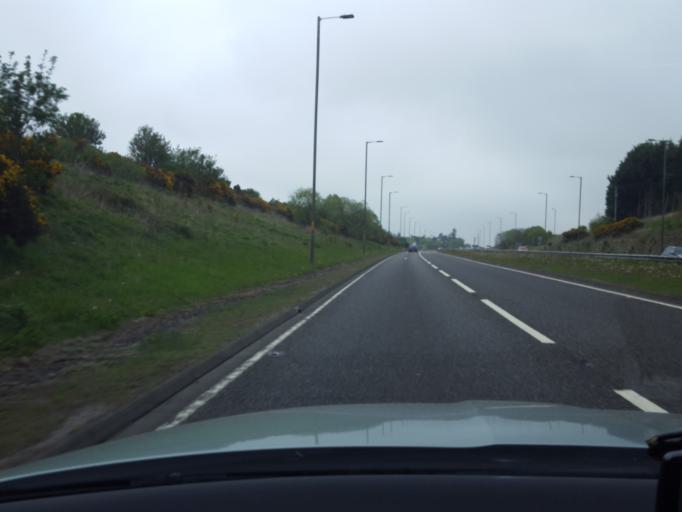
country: GB
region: Scotland
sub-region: Angus
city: Forfar
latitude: 56.6726
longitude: -2.8967
